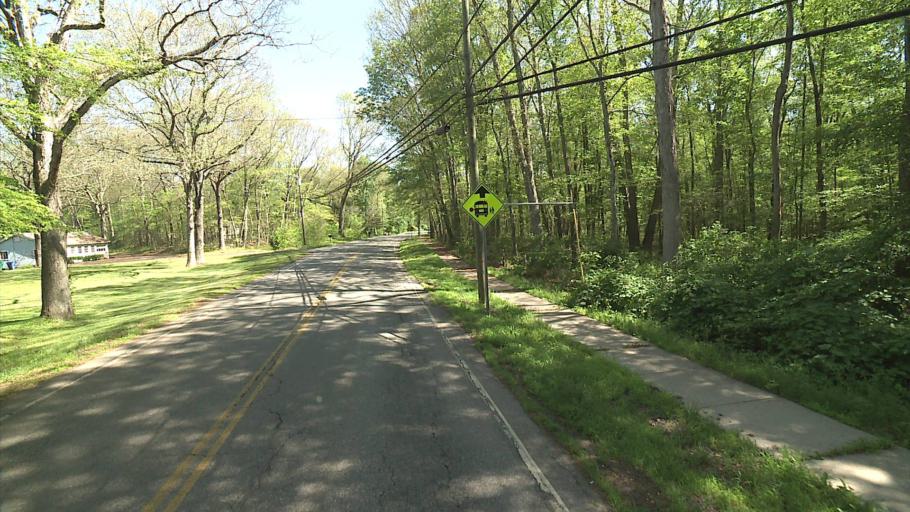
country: US
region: Connecticut
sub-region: New London County
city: Colchester
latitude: 41.5916
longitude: -72.3042
